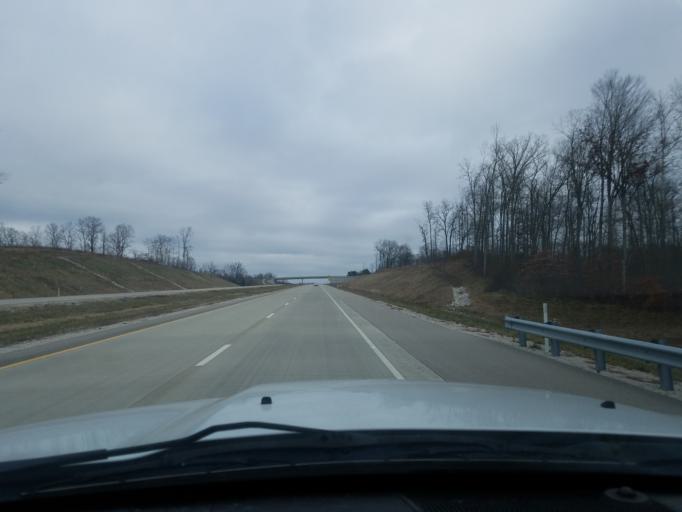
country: US
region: Indiana
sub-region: Monroe County
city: Ellettsville
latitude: 39.0699
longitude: -86.6684
